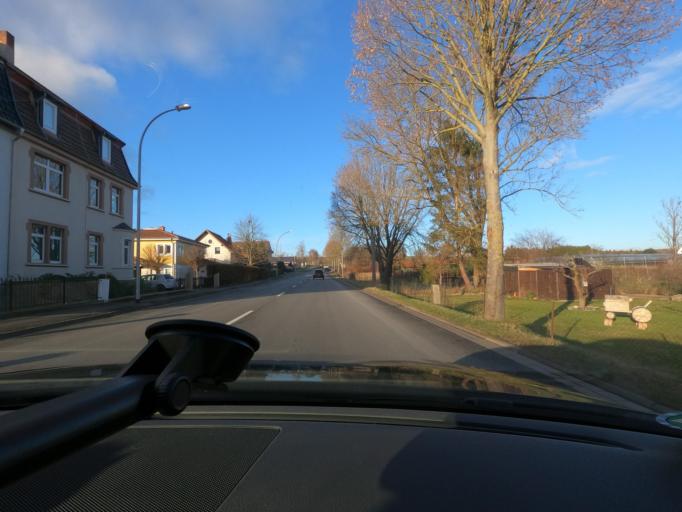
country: DE
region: Lower Saxony
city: Duderstadt
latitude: 51.5184
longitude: 10.2607
